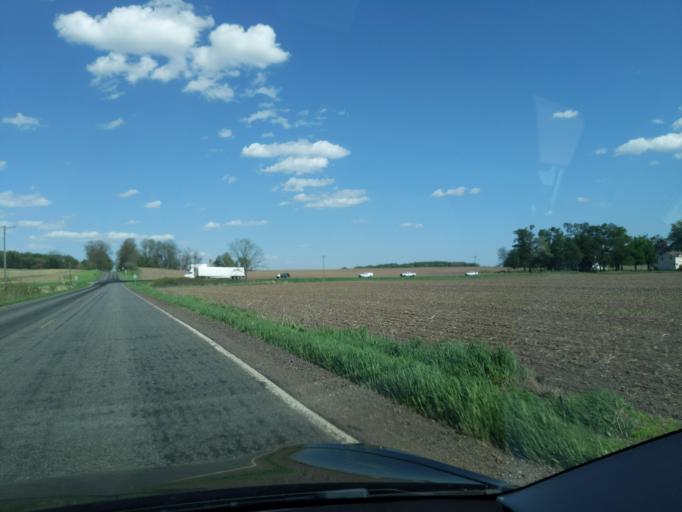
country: US
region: Michigan
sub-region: Kent County
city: Lowell
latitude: 42.7987
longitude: -85.2939
